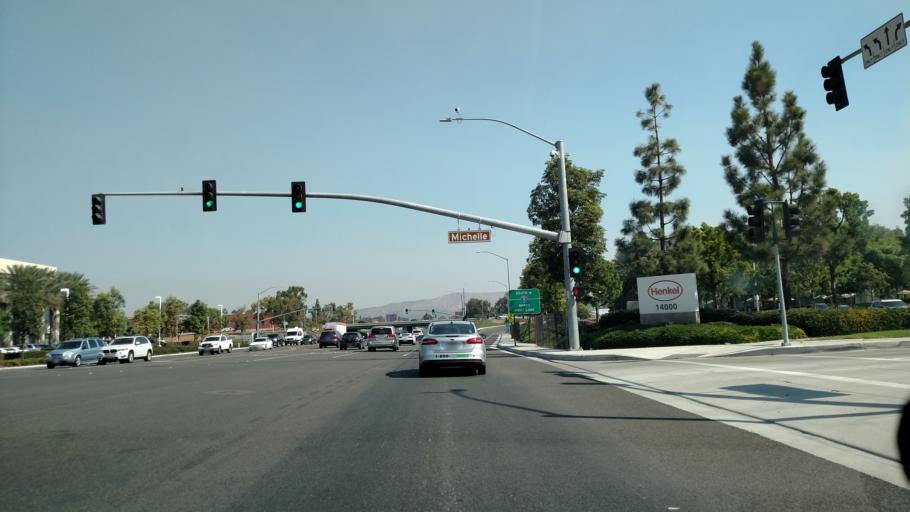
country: US
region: California
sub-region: Orange County
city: Tustin
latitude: 33.7172
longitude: -117.7973
